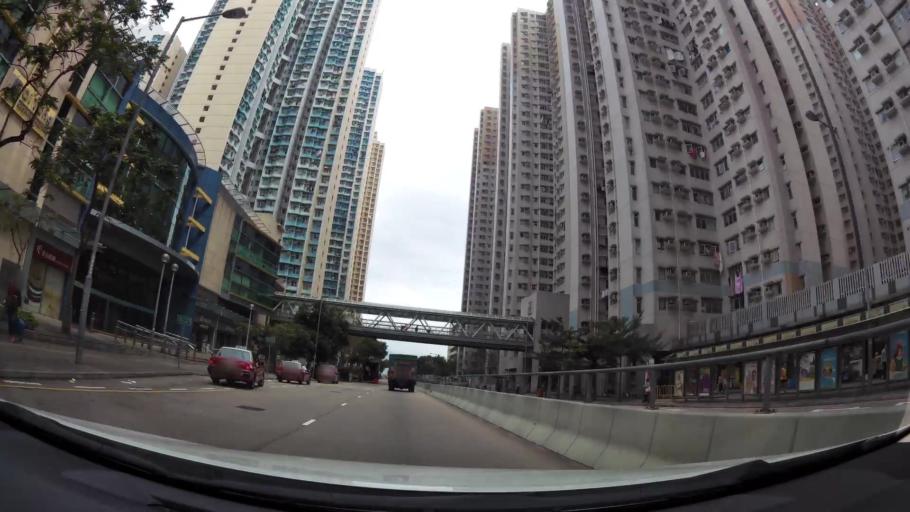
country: HK
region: Wanchai
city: Wan Chai
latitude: 22.2806
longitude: 114.2281
